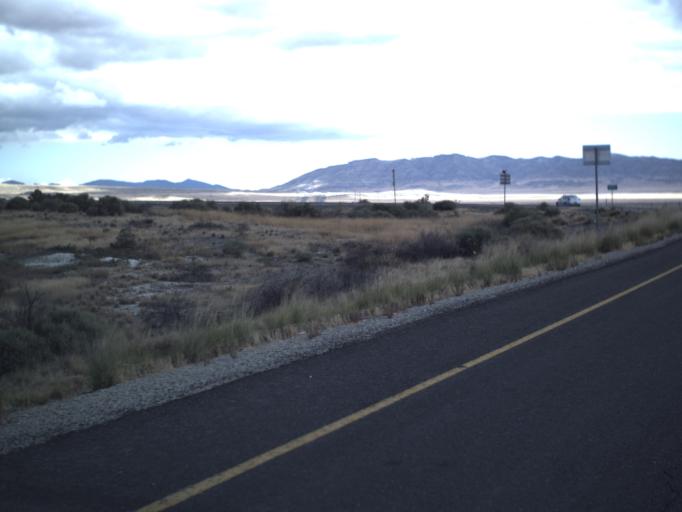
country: US
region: Utah
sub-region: Tooele County
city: Grantsville
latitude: 40.7303
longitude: -113.1144
